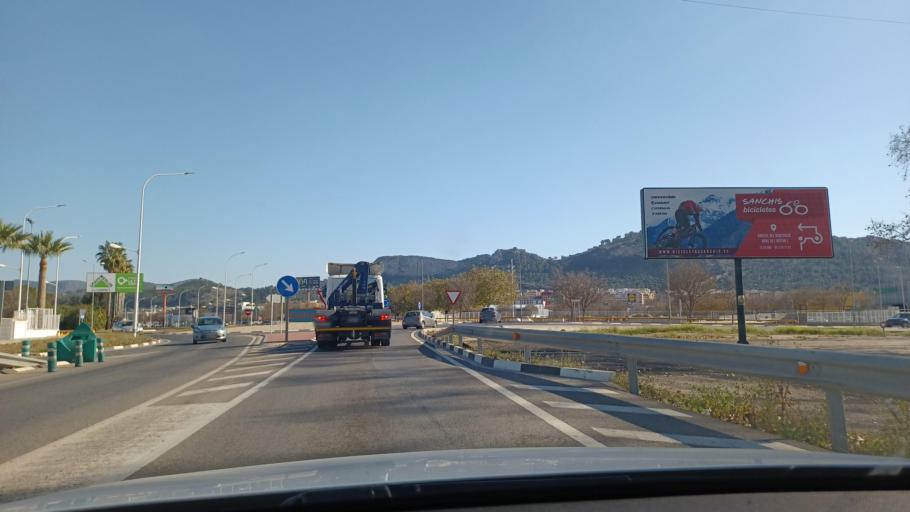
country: ES
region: Valencia
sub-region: Provincia de Valencia
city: Xativa
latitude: 38.9995
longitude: -0.5267
